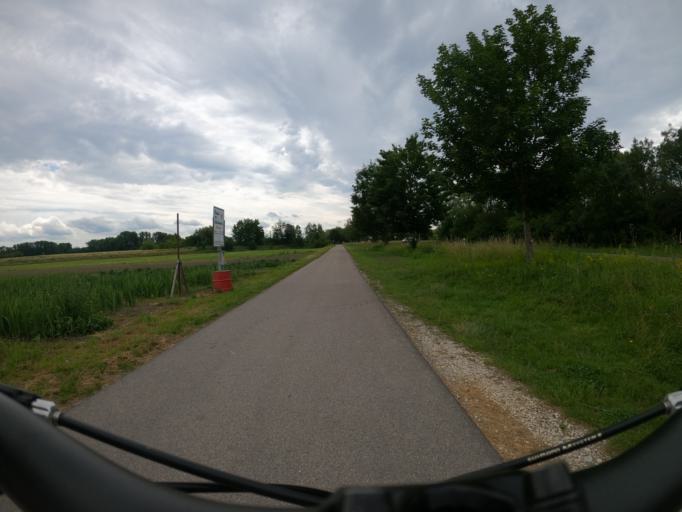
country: DE
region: Bavaria
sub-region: Swabia
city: Holzheim
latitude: 48.4315
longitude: 10.0627
